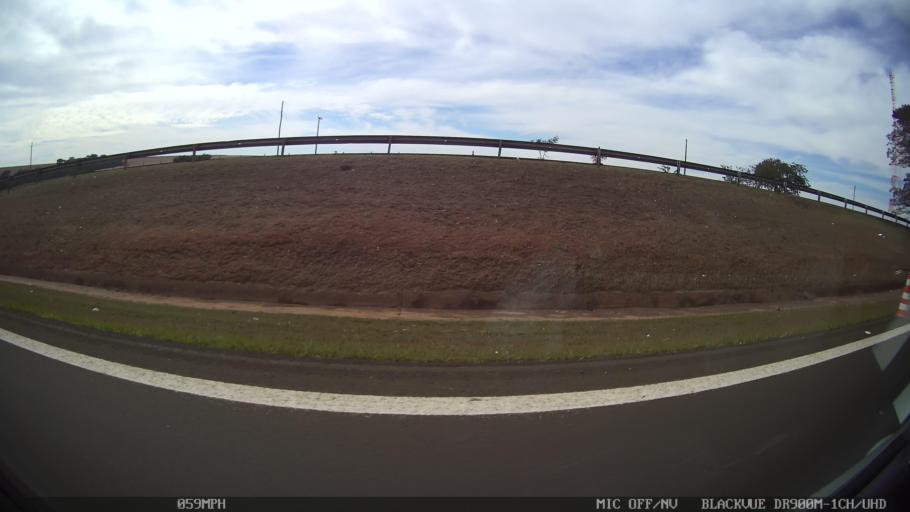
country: BR
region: Sao Paulo
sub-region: Matao
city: Matao
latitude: -21.5660
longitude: -48.4673
